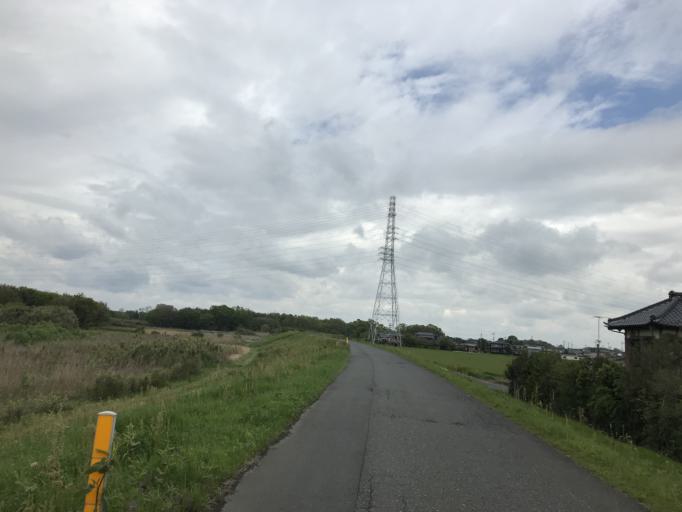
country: JP
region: Ibaraki
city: Mitsukaido
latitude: 36.0078
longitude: 139.9962
